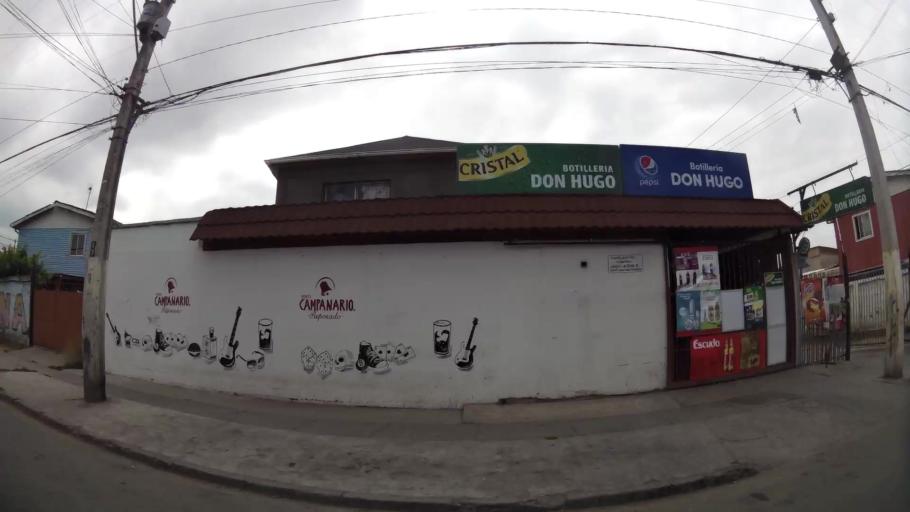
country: CL
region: Santiago Metropolitan
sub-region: Provincia de Santiago
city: Santiago
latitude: -33.5034
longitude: -70.6852
